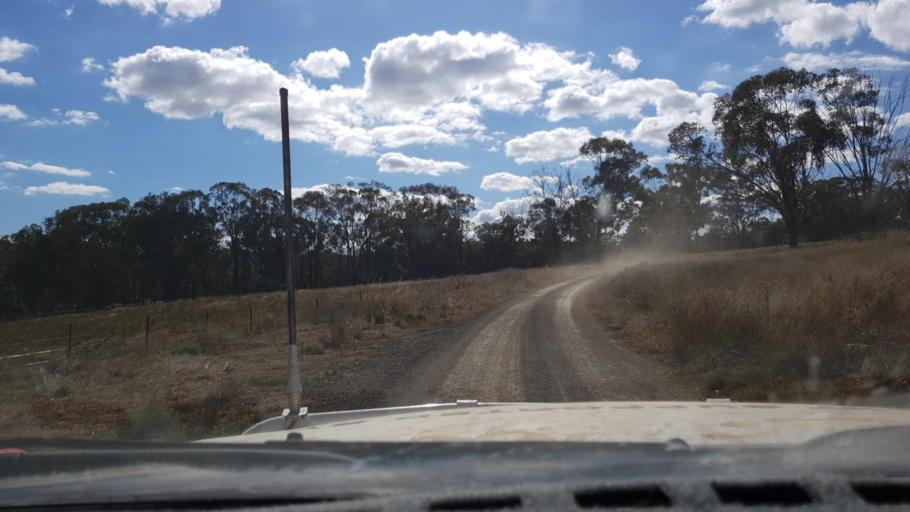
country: AU
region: New South Wales
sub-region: Tamworth Municipality
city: Manilla
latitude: -30.4641
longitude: 150.7788
